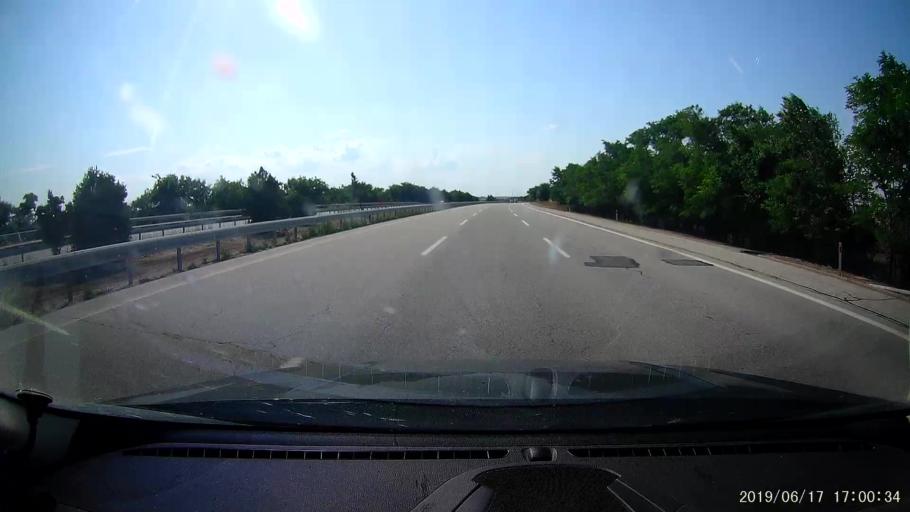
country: TR
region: Edirne
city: Haskoy
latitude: 41.6223
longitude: 26.8265
